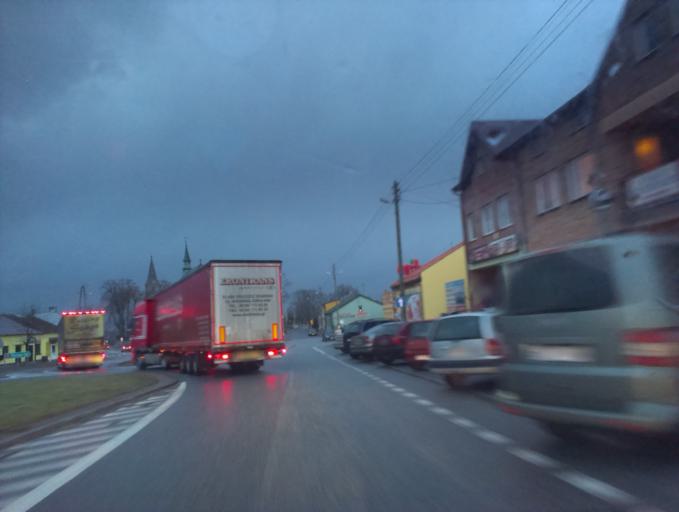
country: PL
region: Lodz Voivodeship
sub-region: Powiat opoczynski
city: Zarnow
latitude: 51.2473
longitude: 20.1720
